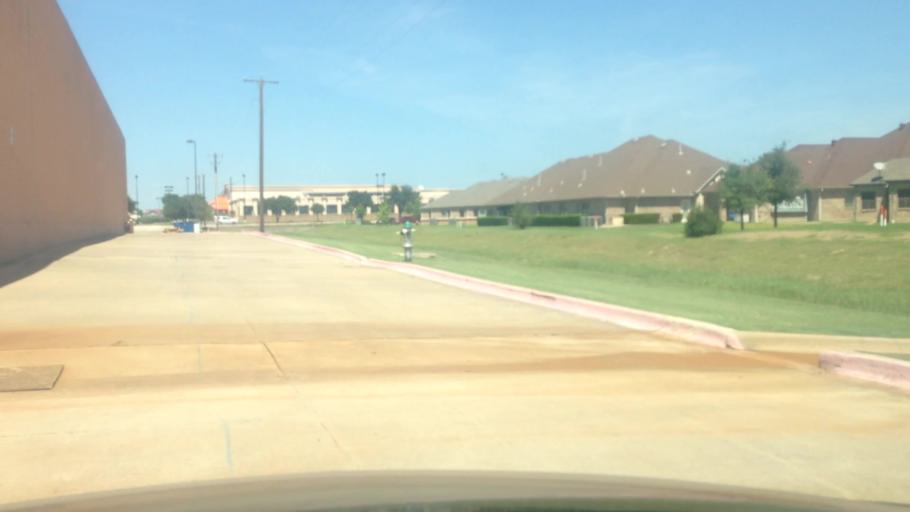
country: US
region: Texas
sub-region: Tarrant County
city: Watauga
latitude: 32.8928
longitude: -97.2562
